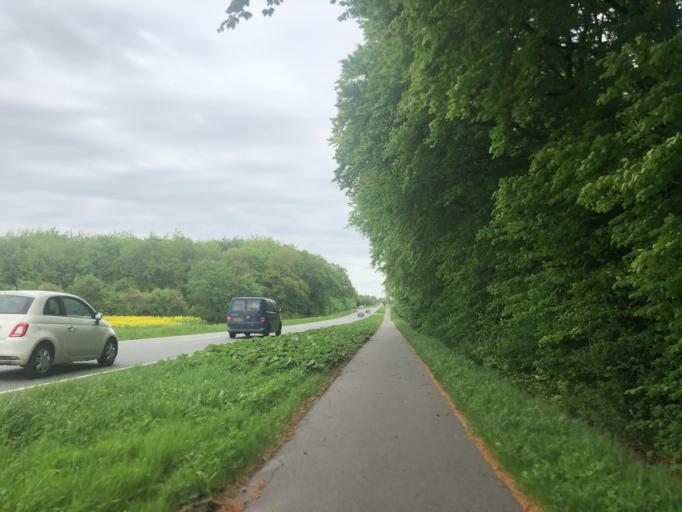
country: DK
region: Zealand
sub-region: Koge Kommune
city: Borup
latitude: 55.4472
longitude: 11.9248
